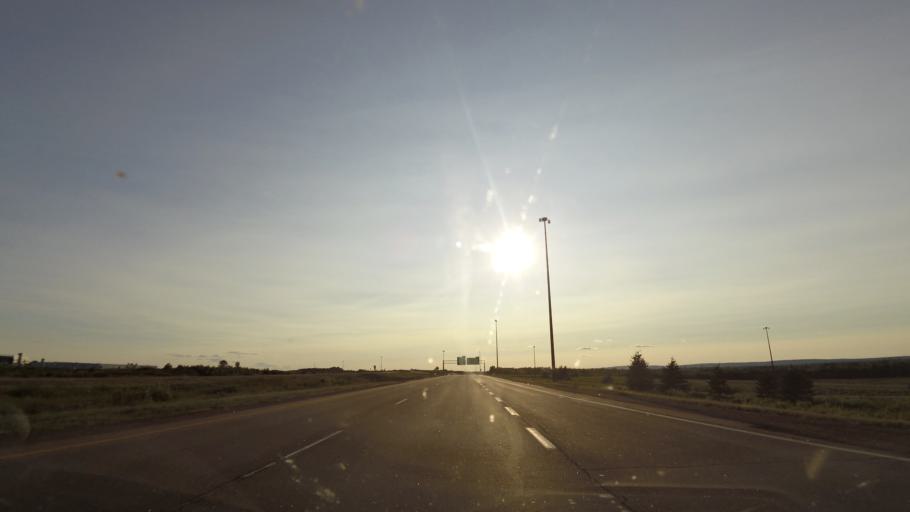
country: CA
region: New Brunswick
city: Dieppe
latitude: 46.1288
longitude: -64.6756
